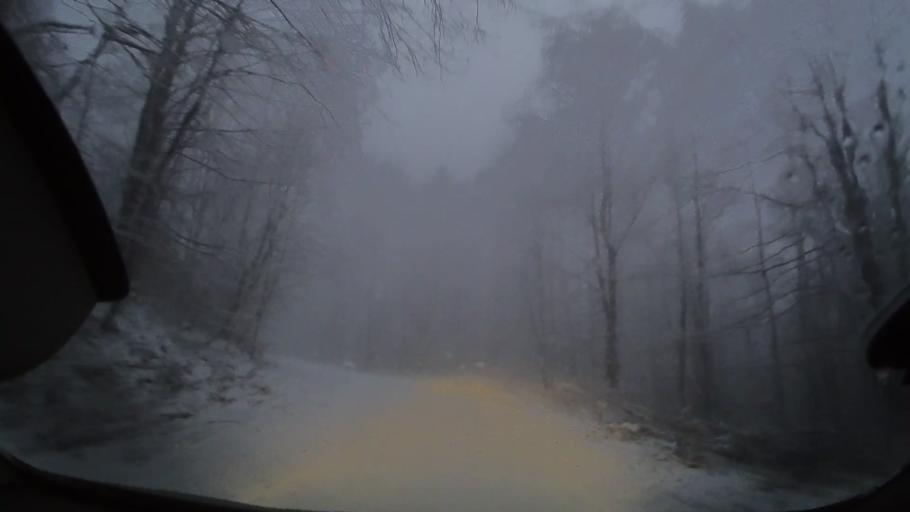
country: RO
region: Alba
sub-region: Comuna Avram Iancu
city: Avram Iancu
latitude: 46.3125
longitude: 22.8058
